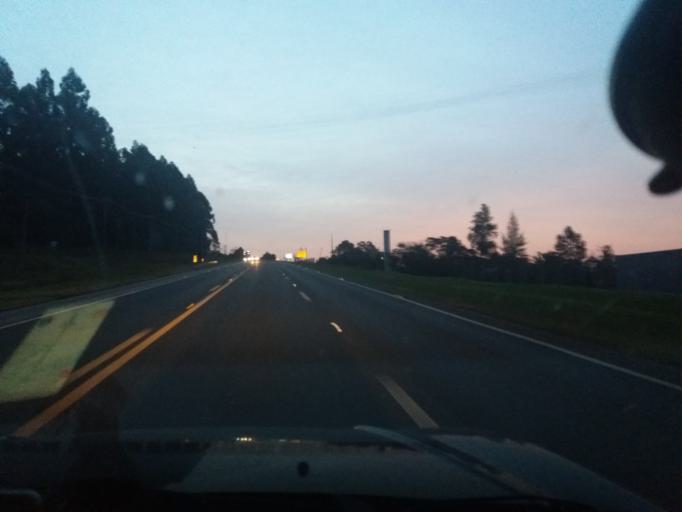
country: BR
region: Sao Paulo
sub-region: Itapeva
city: Itapeva
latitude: -23.9759
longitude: -48.8544
